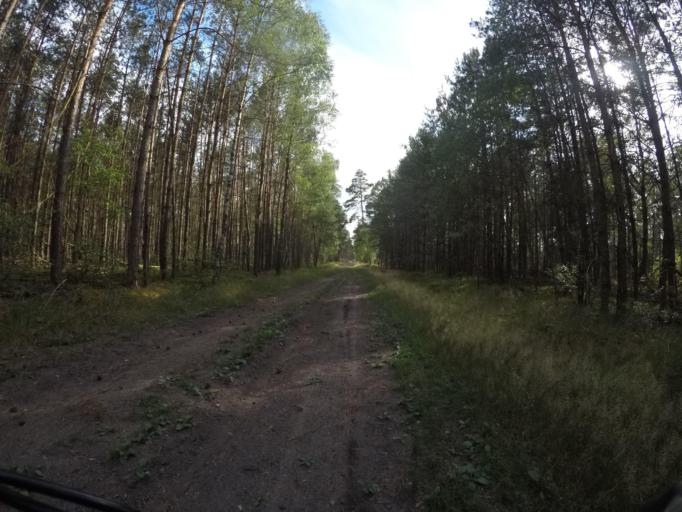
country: DE
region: Lower Saxony
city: Neu Darchau
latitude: 53.2727
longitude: 10.9647
